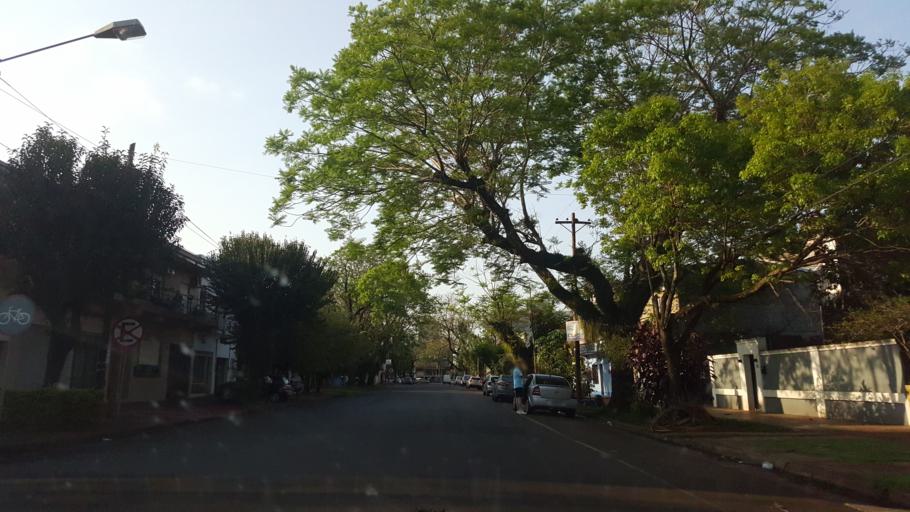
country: AR
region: Misiones
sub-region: Departamento de Capital
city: Posadas
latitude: -27.3768
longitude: -55.8951
